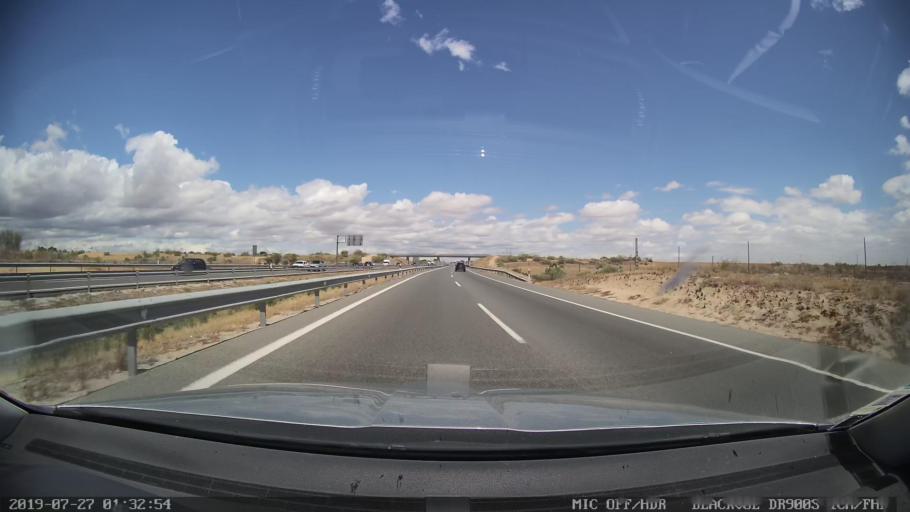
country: ES
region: Castille-La Mancha
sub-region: Province of Toledo
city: Valmojado
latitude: 40.2265
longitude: -4.0722
